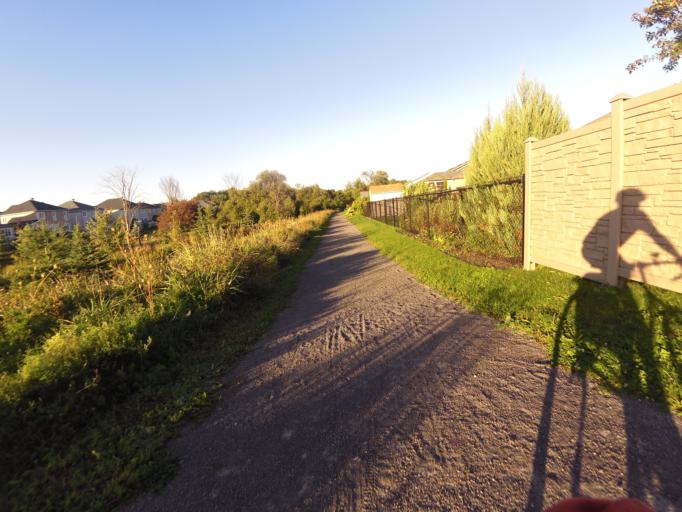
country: CA
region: Ontario
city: Bells Corners
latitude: 45.3598
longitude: -75.9283
